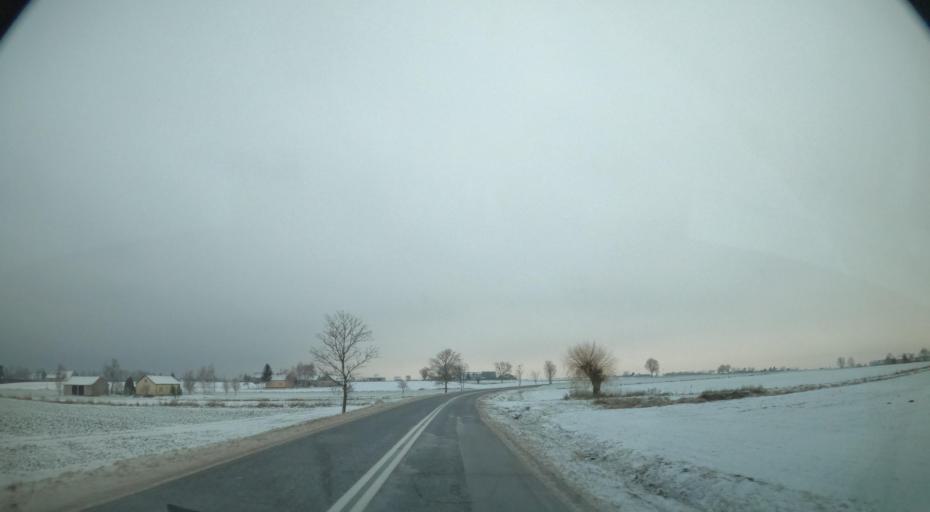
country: PL
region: Kujawsko-Pomorskie
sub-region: Powiat lipnowski
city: Dobrzyn nad Wisla
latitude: 52.6365
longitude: 19.4037
